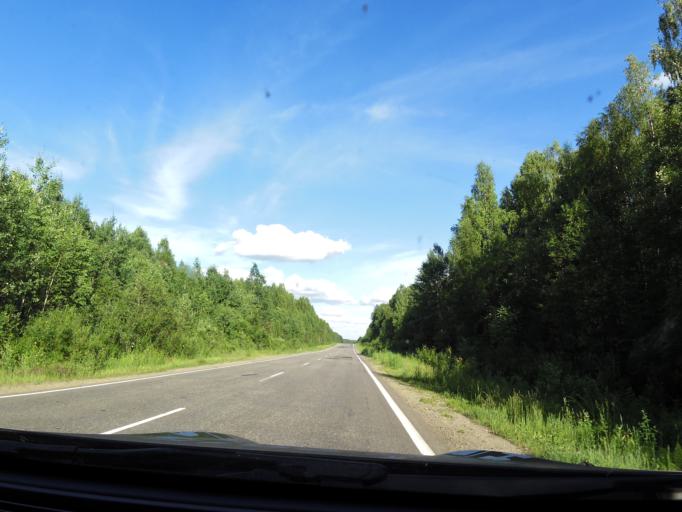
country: RU
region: Kirov
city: Omutninsk
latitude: 58.7593
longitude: 52.0171
